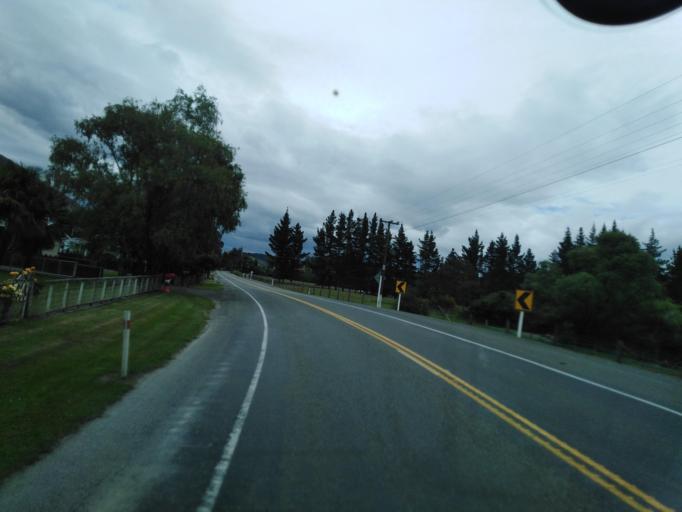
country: NZ
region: Tasman
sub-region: Tasman District
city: Wakefield
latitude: -41.4507
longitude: 172.9581
